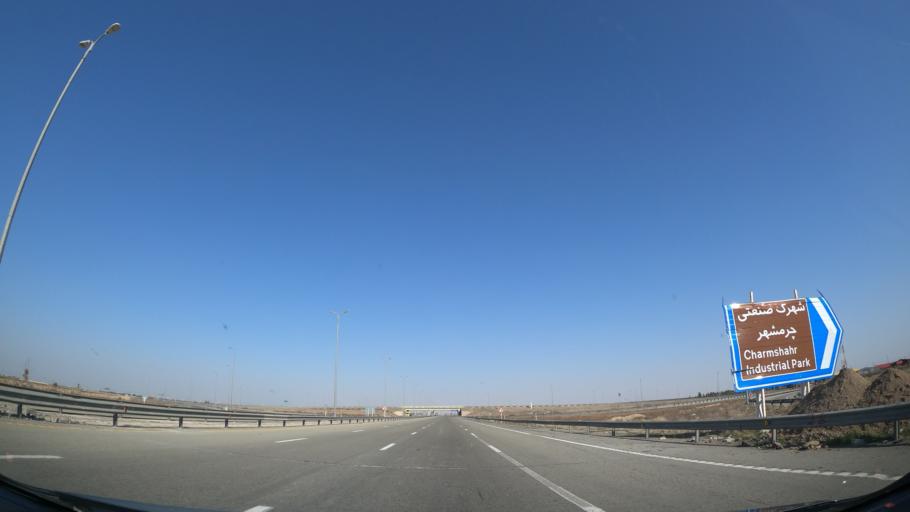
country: IR
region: Tehran
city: Eqbaliyeh
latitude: 35.1411
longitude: 51.5304
